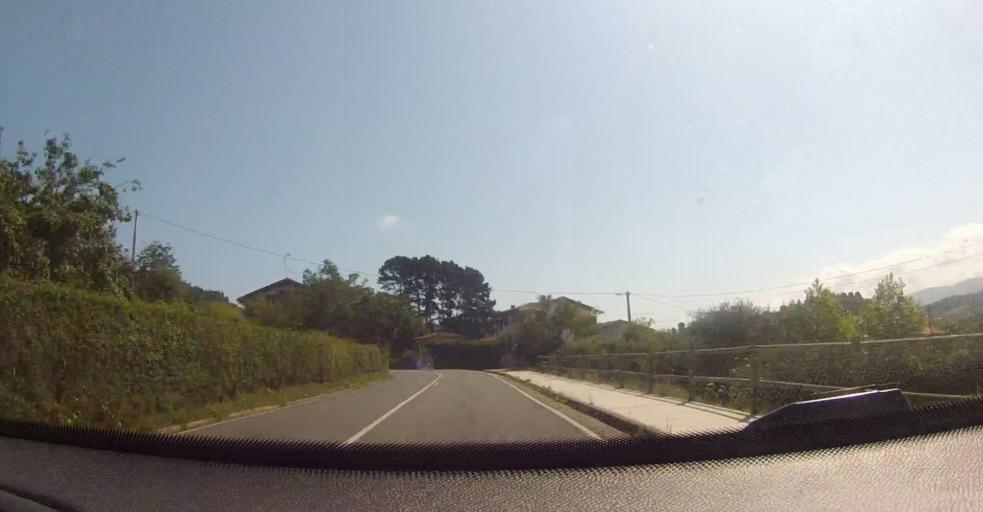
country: ES
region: Asturias
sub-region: Province of Asturias
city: Colunga
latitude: 43.4884
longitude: -5.2831
